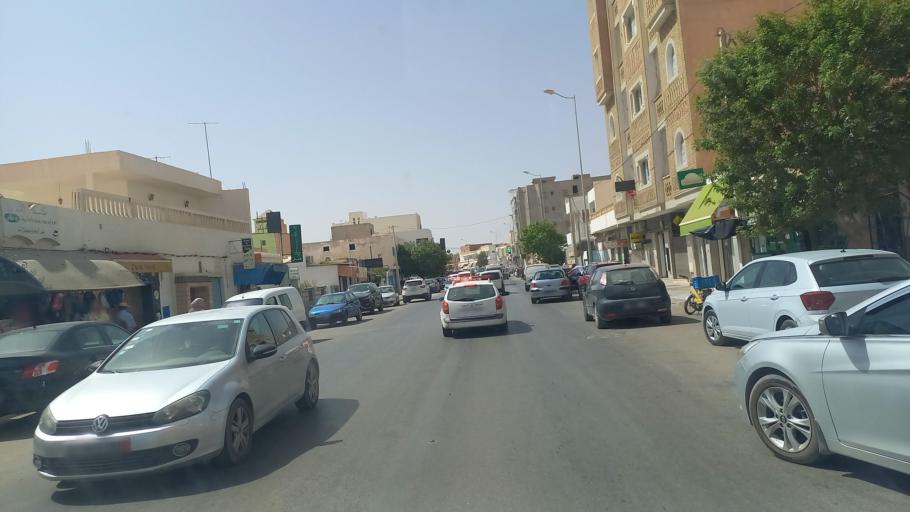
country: TN
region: Madanin
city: Medenine
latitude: 33.3384
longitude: 10.4866
